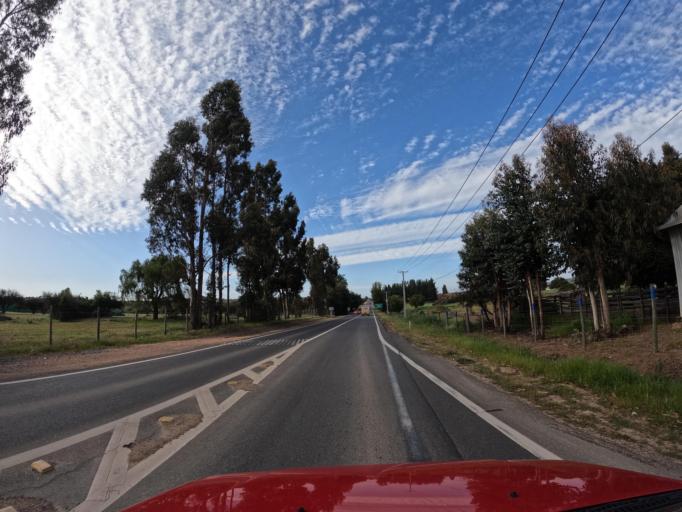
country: CL
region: Valparaiso
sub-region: San Antonio Province
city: San Antonio
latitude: -34.1418
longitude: -71.7304
